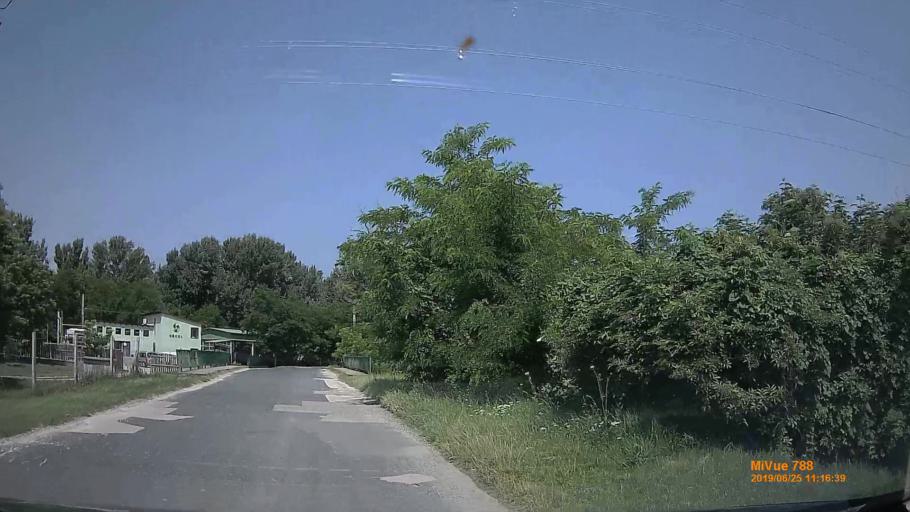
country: HU
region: Komarom-Esztergom
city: Tokod
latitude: 47.7270
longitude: 18.6554
